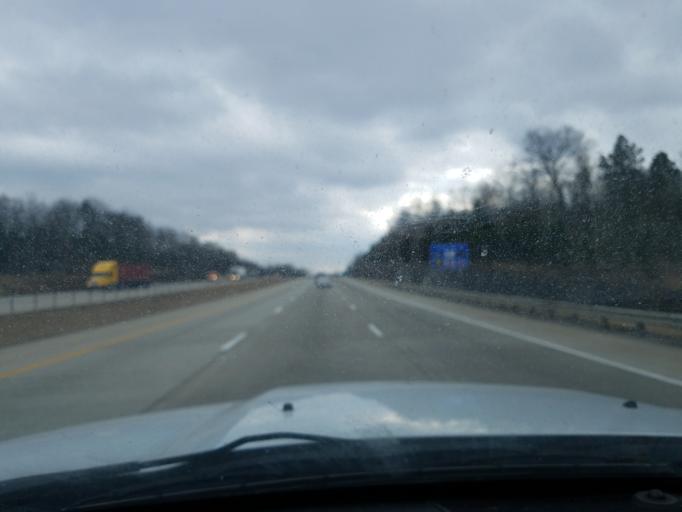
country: US
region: Kentucky
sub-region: Bullitt County
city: Shepherdsville
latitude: 38.0178
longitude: -85.6968
